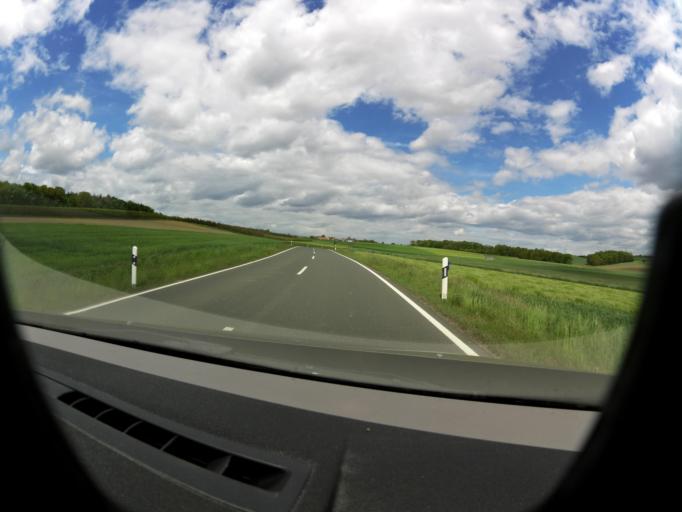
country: DE
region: Bavaria
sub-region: Regierungsbezirk Unterfranken
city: Frickenhausen
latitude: 49.6948
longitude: 10.0826
